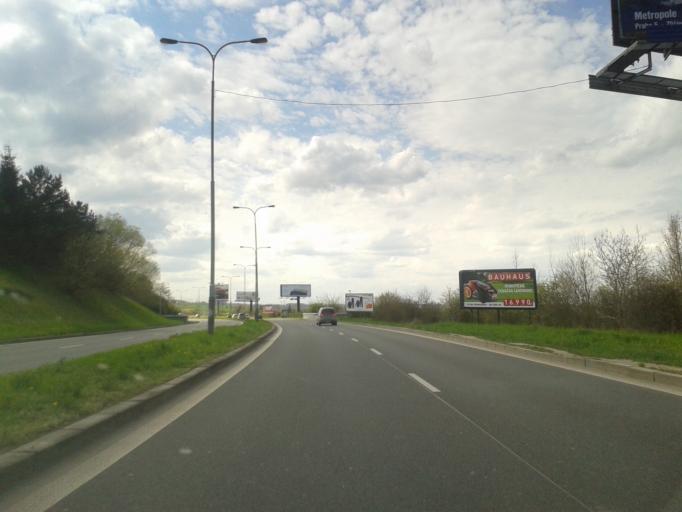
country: CZ
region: Praha
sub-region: Praha 12
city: Modrany
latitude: 50.0265
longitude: 14.3635
